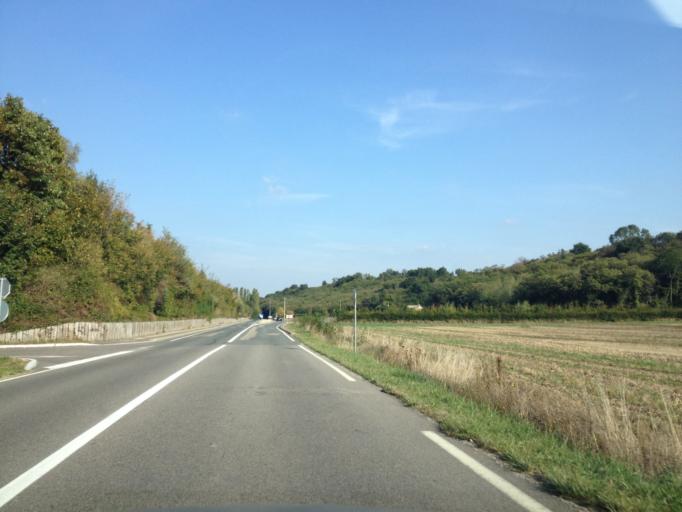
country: FR
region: Rhone-Alpes
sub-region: Departement de l'Isere
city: Villefontaine
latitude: 45.6020
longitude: 5.1422
